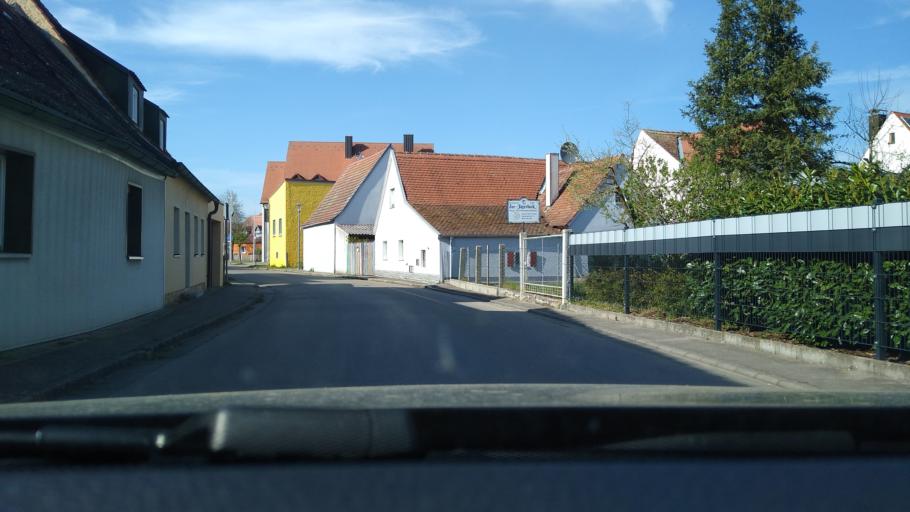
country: DE
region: Bavaria
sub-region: Regierungsbezirk Mittelfranken
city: Muhr am See
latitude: 49.1544
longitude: 10.7119
